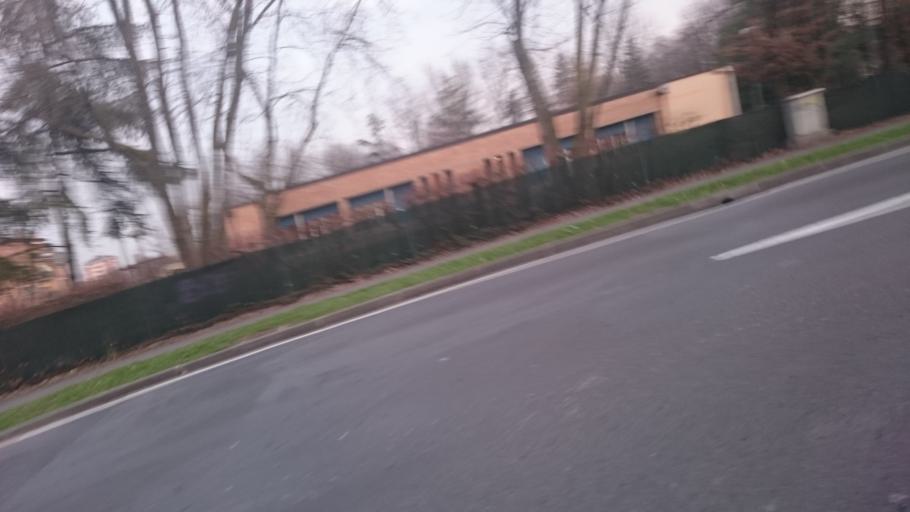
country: IT
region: Emilia-Romagna
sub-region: Provincia di Reggio Emilia
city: Reggio nell'Emilia
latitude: 44.7150
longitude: 10.6339
